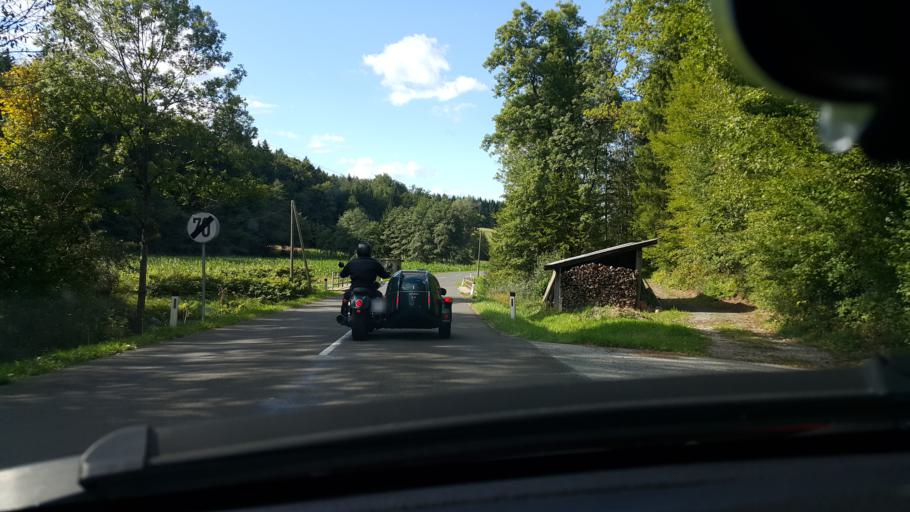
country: AT
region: Styria
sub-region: Politischer Bezirk Leibnitz
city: Leutschach
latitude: 46.6521
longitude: 15.4877
